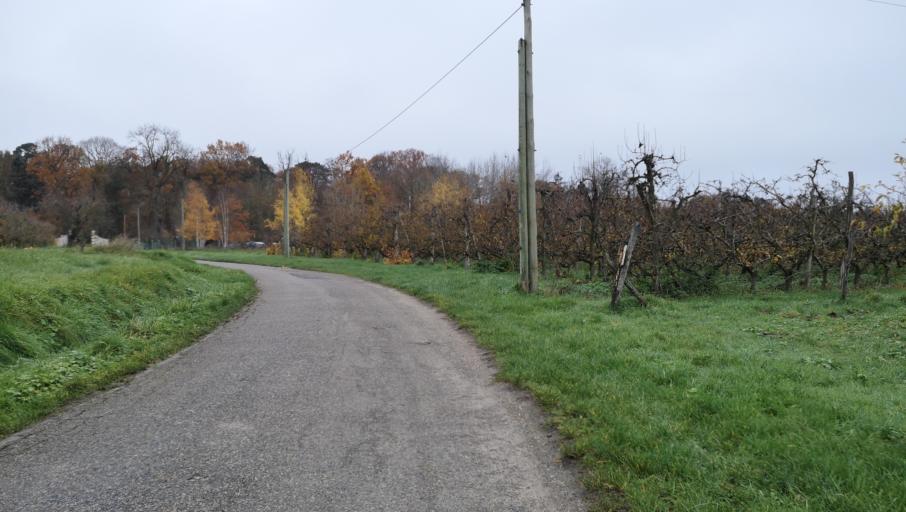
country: FR
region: Centre
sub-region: Departement du Loiret
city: Saint-Jean-de-Braye
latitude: 47.9290
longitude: 1.9771
